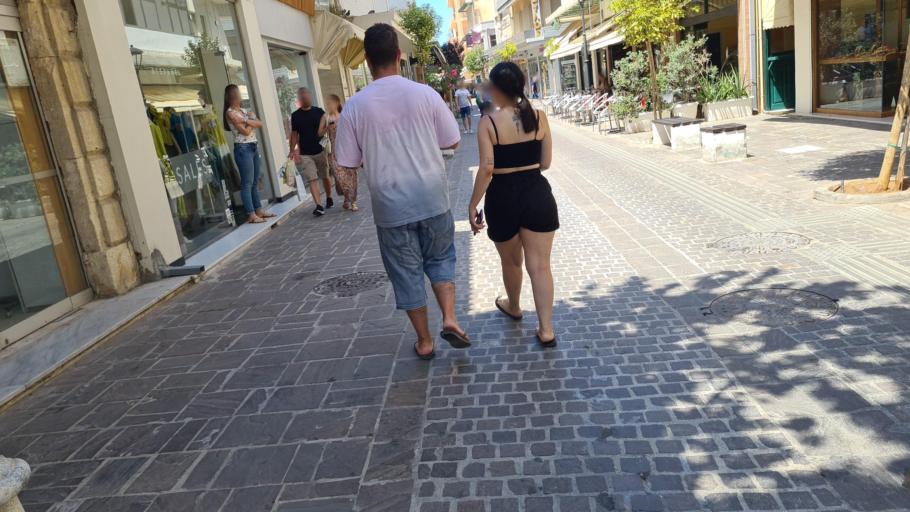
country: GR
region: Crete
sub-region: Nomos Chanias
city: Chania
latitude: 35.5150
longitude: 24.0199
